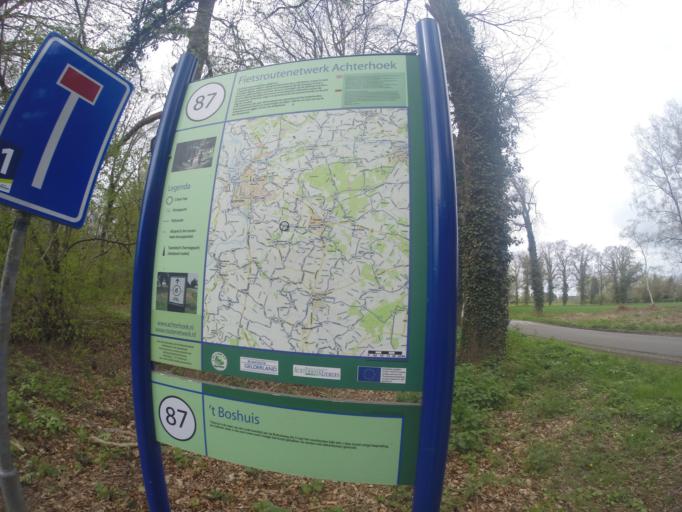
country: NL
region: Gelderland
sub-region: Gemeente Zutphen
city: Leesten
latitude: 52.1033
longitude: 6.2667
